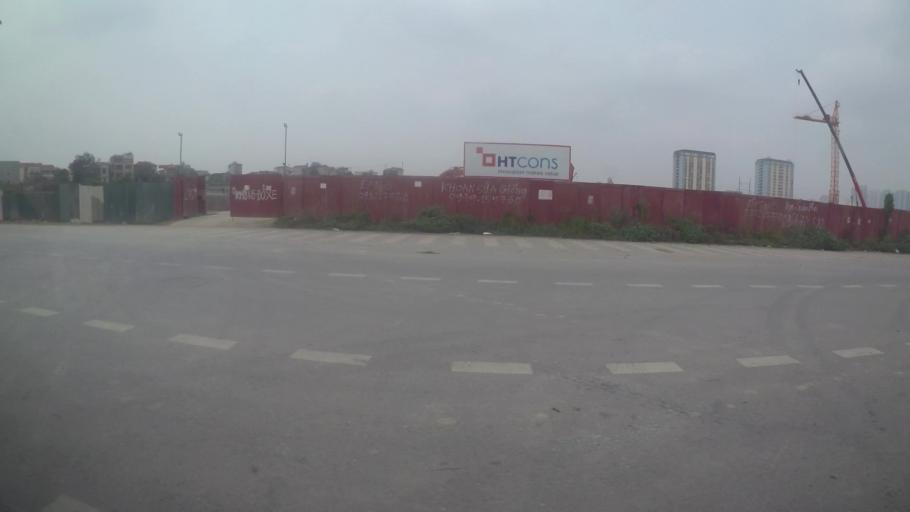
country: VN
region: Ha Noi
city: Cau Dien
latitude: 21.0381
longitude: 105.7458
